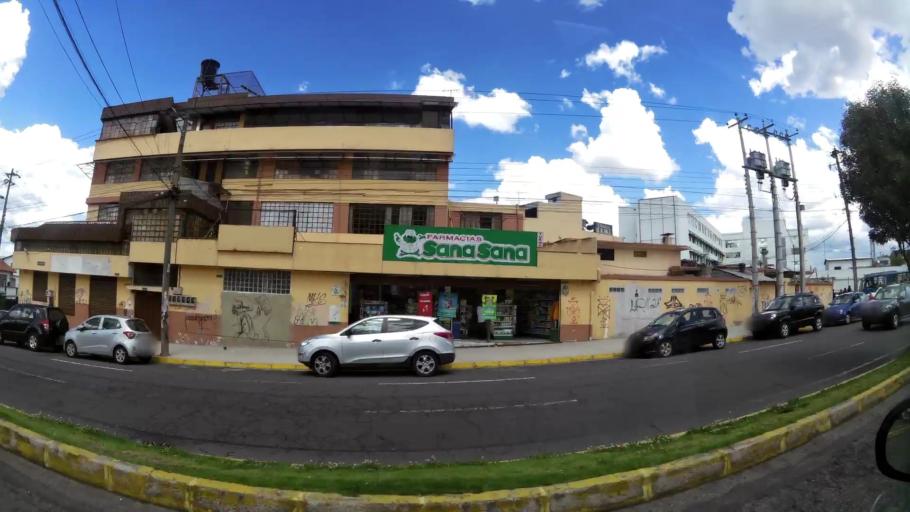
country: EC
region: Pichincha
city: Quito
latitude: -0.2039
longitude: -78.5053
